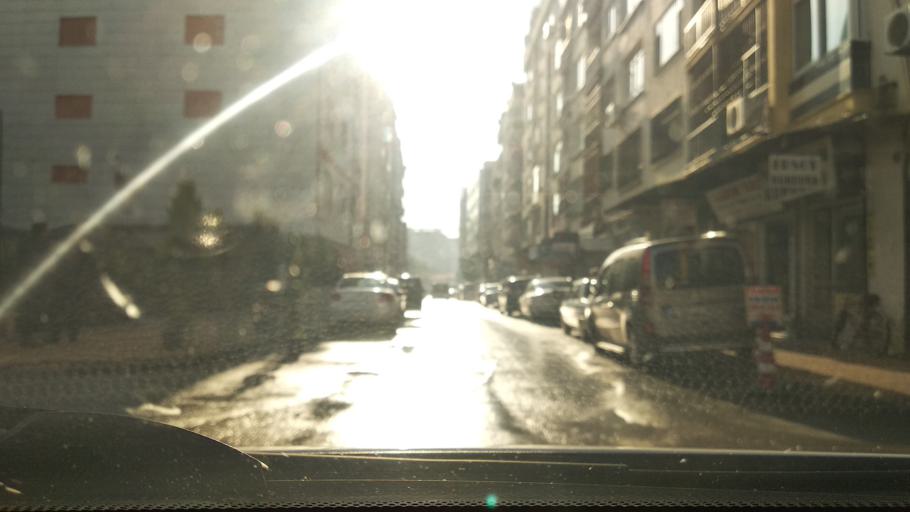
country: TR
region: Mersin
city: Mercin
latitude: 36.8066
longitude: 34.6215
